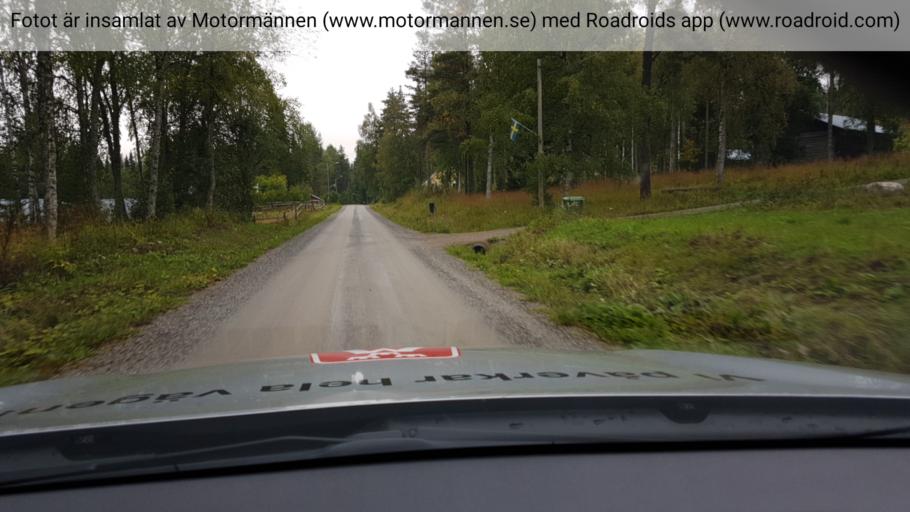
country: SE
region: Jaemtland
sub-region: Braecke Kommun
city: Braecke
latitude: 62.7536
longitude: 15.5034
